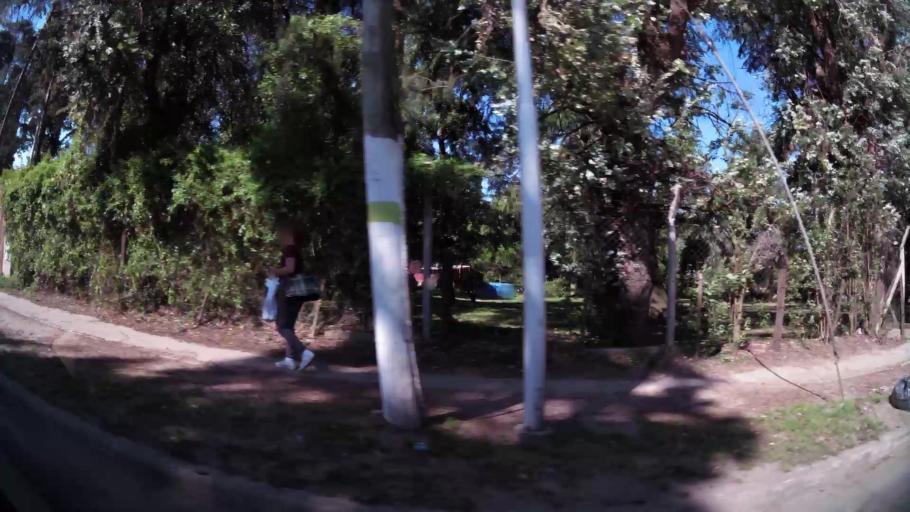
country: AR
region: Buenos Aires
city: Santa Catalina - Dique Lujan
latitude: -34.4870
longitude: -58.6951
